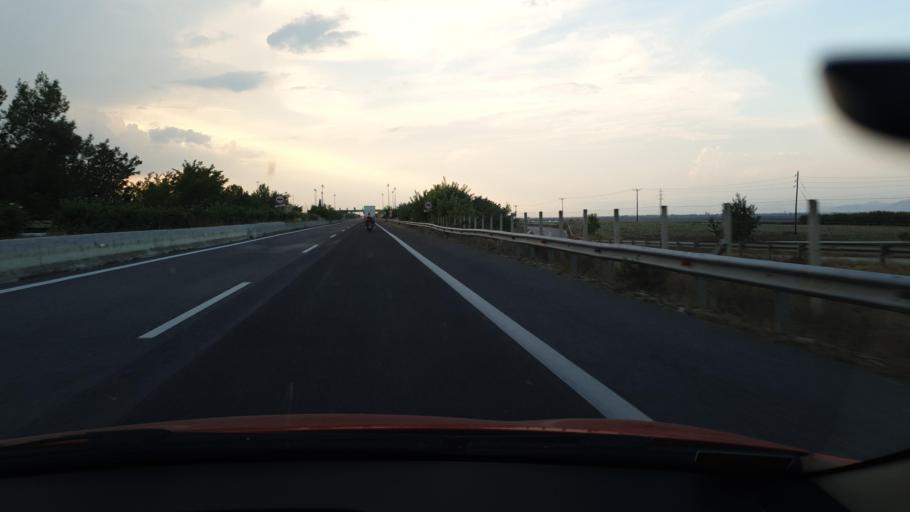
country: GR
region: Thessaly
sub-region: Nomos Larisis
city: Chalki
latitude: 39.5192
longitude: 22.5624
